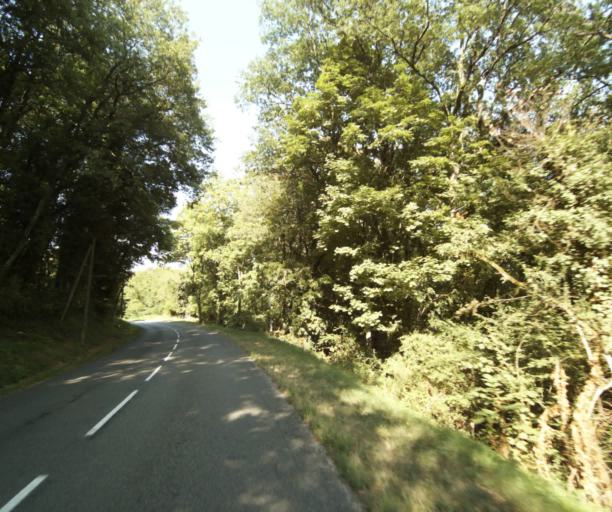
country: FR
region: Bourgogne
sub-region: Departement de Saone-et-Loire
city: Tournus
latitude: 46.5584
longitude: 4.8773
